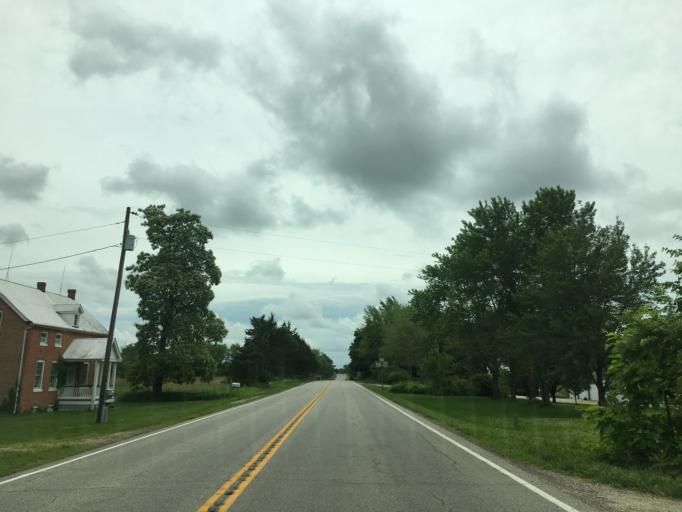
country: US
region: Missouri
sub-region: Gasconade County
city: Owensville
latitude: 38.4719
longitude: -91.4647
